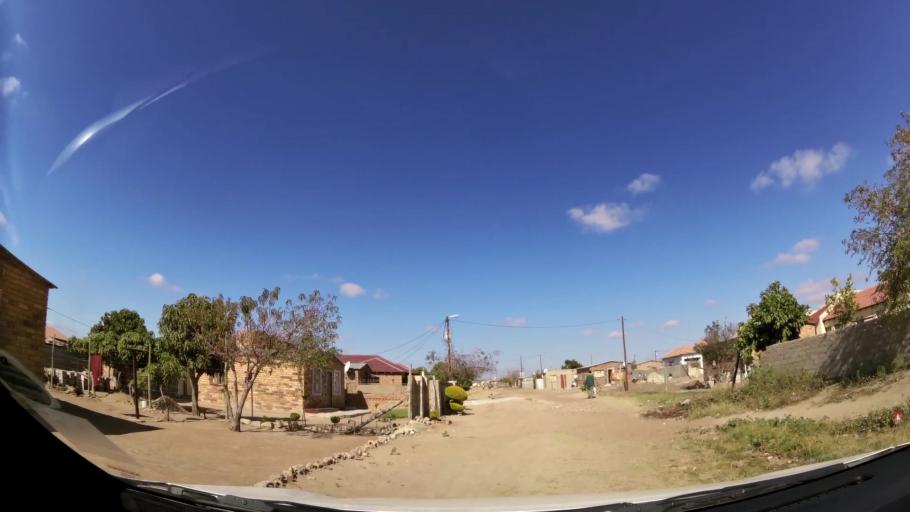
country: ZA
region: Limpopo
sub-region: Capricorn District Municipality
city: Polokwane
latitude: -23.8576
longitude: 29.3987
